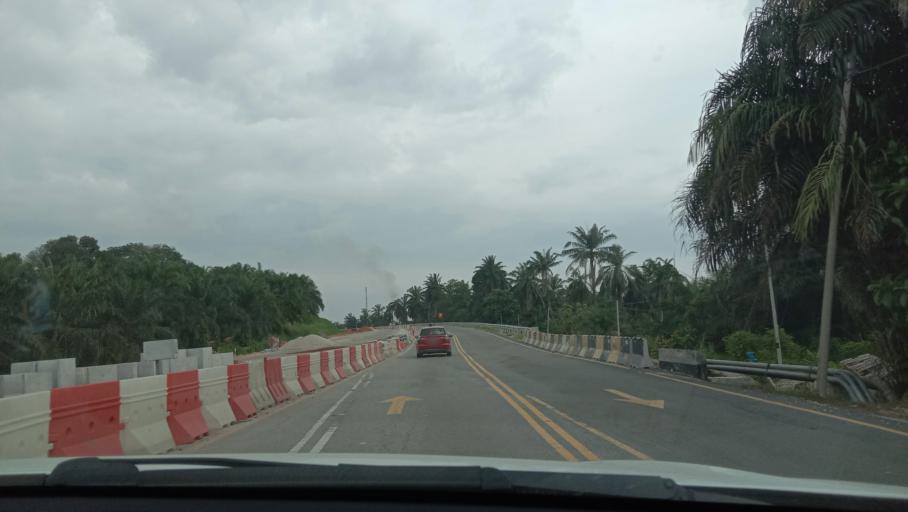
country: MY
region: Selangor
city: Batu Arang
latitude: 3.2710
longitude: 101.4540
